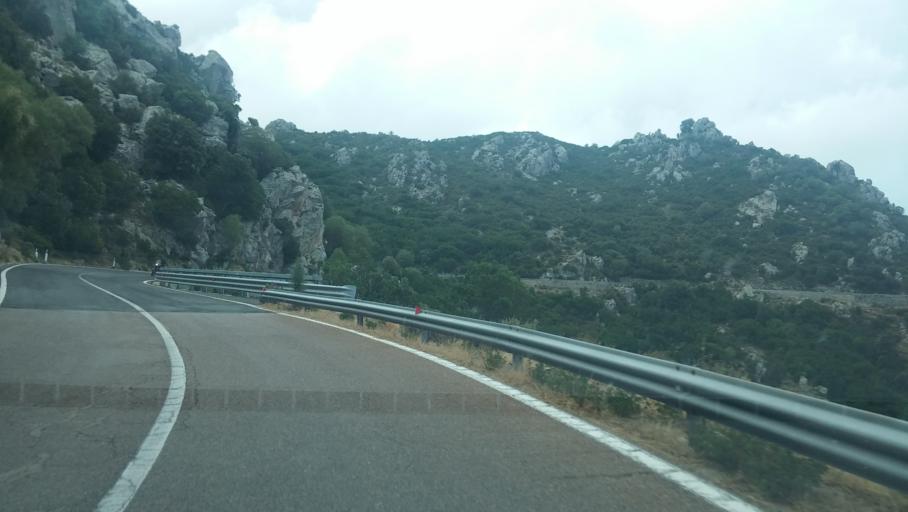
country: IT
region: Sardinia
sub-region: Provincia di Ogliastra
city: Urzulei
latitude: 40.1818
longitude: 9.5327
